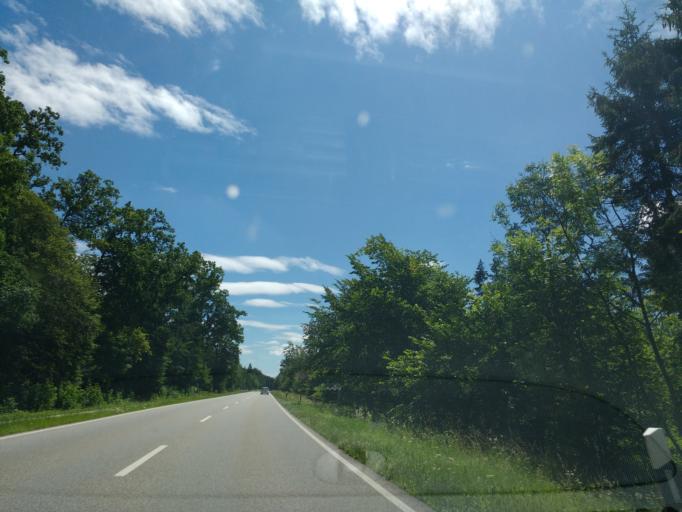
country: DE
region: Bavaria
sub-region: Upper Bavaria
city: Kastl
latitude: 48.2233
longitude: 12.7228
